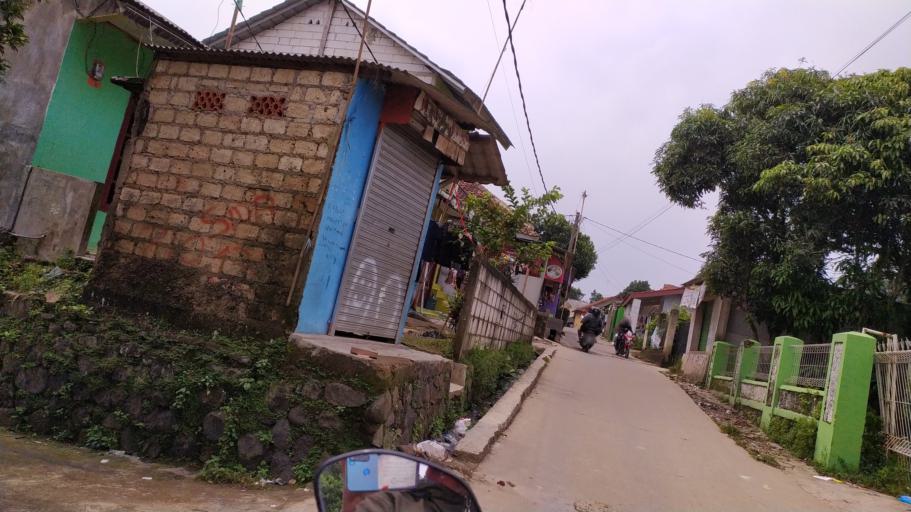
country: ID
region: West Java
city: Ciampea
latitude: -6.5796
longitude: 106.7237
